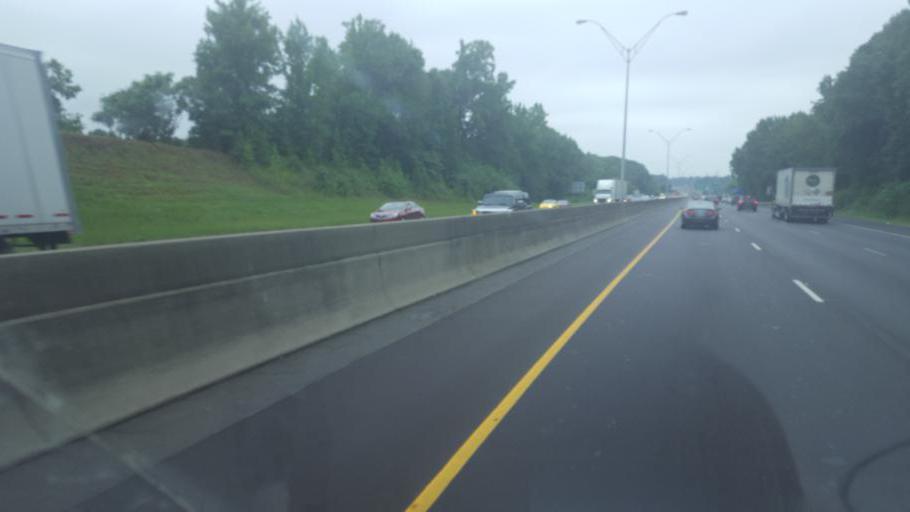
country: US
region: North Carolina
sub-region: Mecklenburg County
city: Pineville
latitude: 35.1536
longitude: -80.8932
